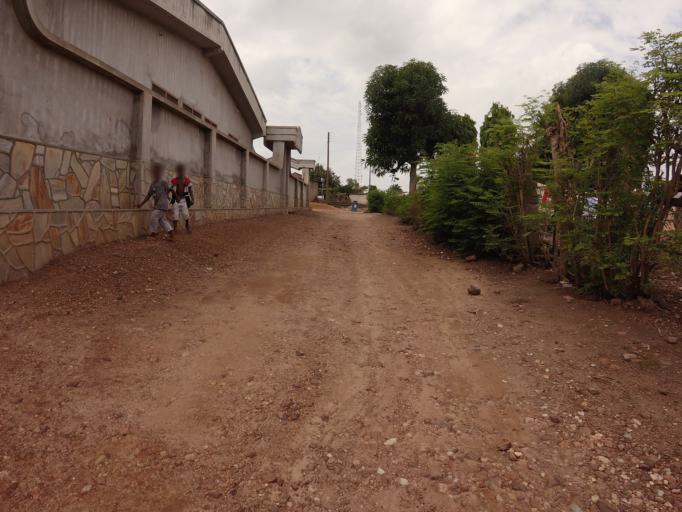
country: GH
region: Volta
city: Ho
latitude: 6.6006
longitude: 0.4695
